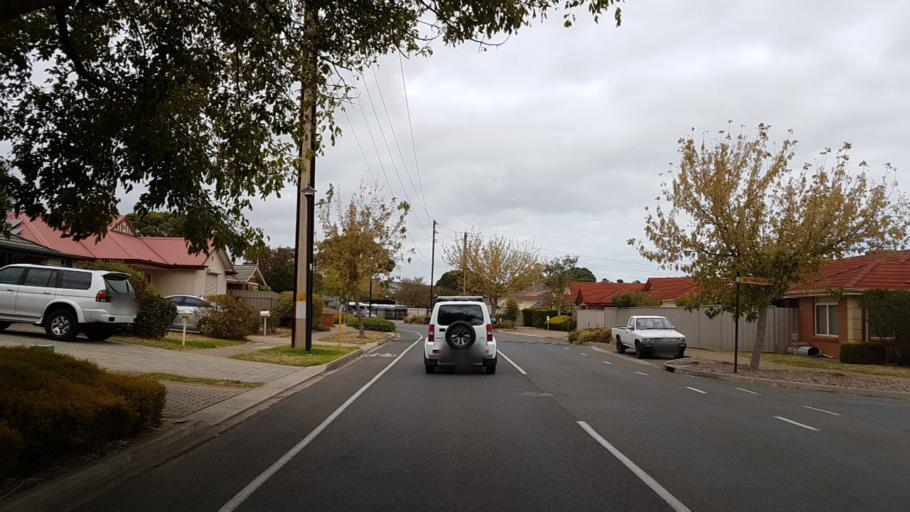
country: AU
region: South Australia
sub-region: Marion
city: Marion
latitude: -35.0155
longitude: 138.5646
